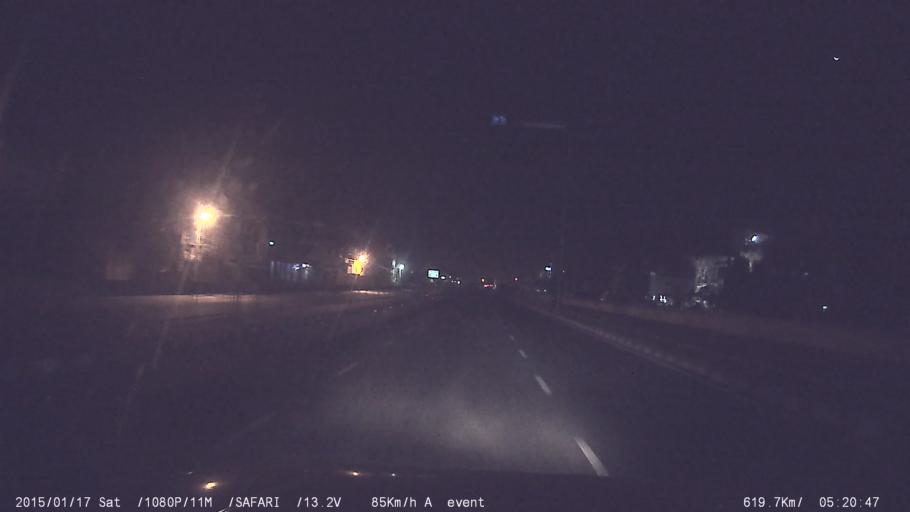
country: IN
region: Tamil Nadu
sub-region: Vellore
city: Vellore
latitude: 12.9377
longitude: 79.1632
